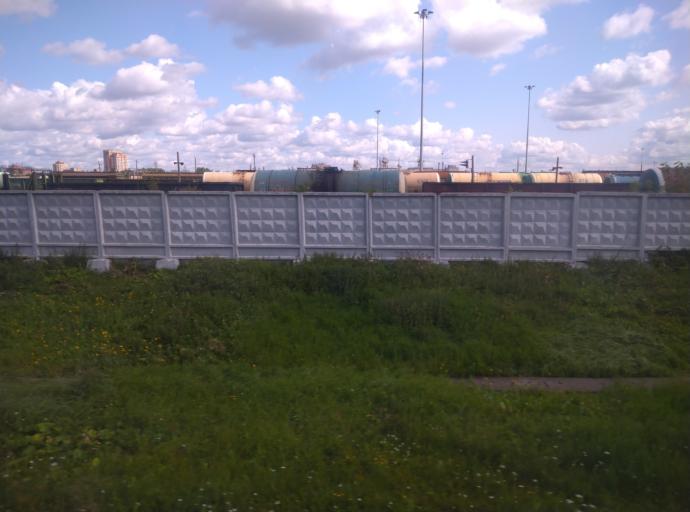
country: RU
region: St.-Petersburg
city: Obukhovo
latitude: 59.8743
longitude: 30.4142
